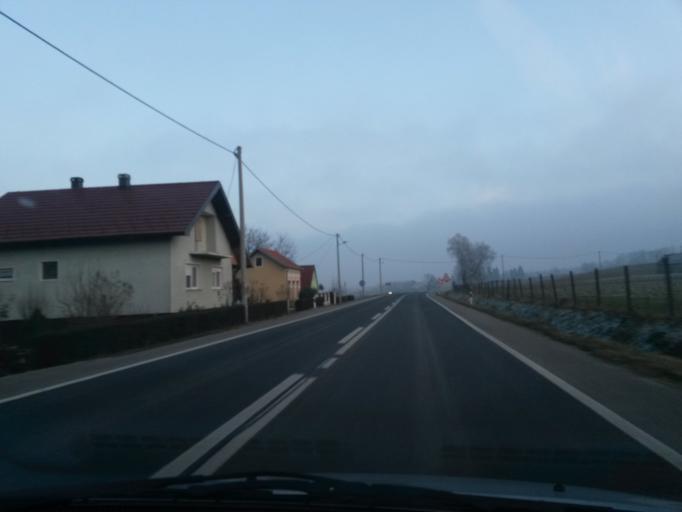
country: HR
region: Varazdinska
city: Ludbreg
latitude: 46.2166
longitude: 16.6870
